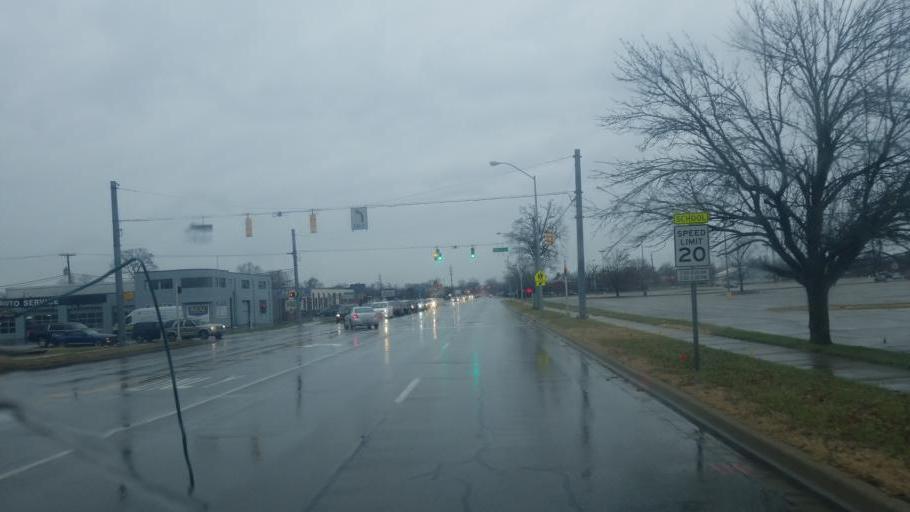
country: US
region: Indiana
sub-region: Bartholomew County
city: Columbus
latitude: 39.2231
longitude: -85.8985
